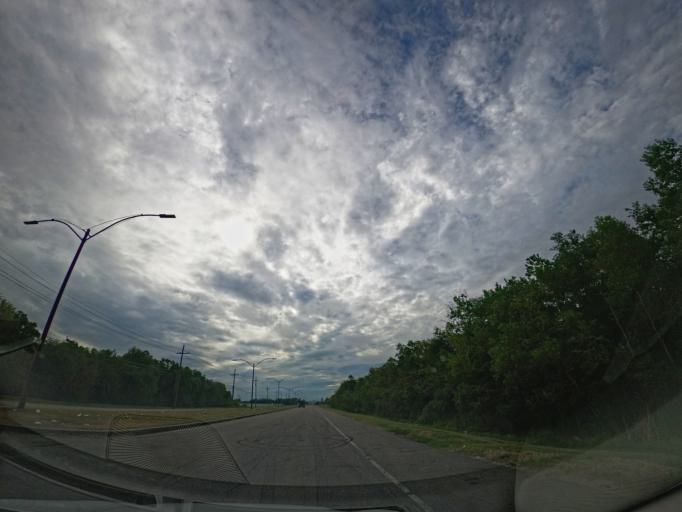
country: US
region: Louisiana
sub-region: Saint Bernard Parish
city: Arabi
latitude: 30.0056
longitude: -90.0069
